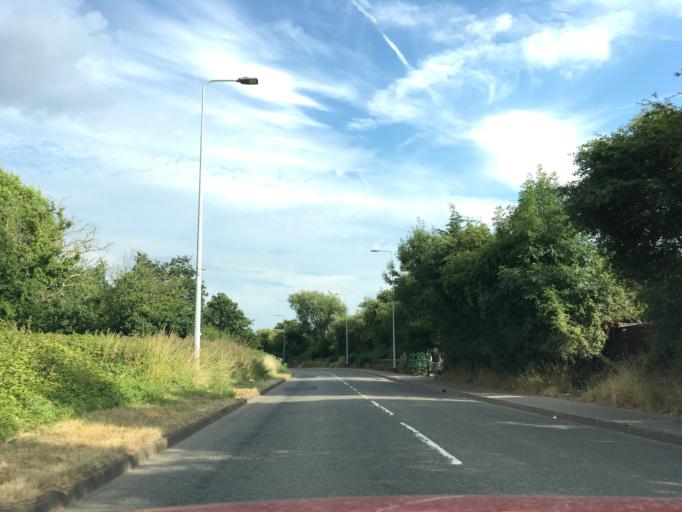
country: GB
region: Wales
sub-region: Newport
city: Marshfield
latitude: 51.5212
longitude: -3.1063
